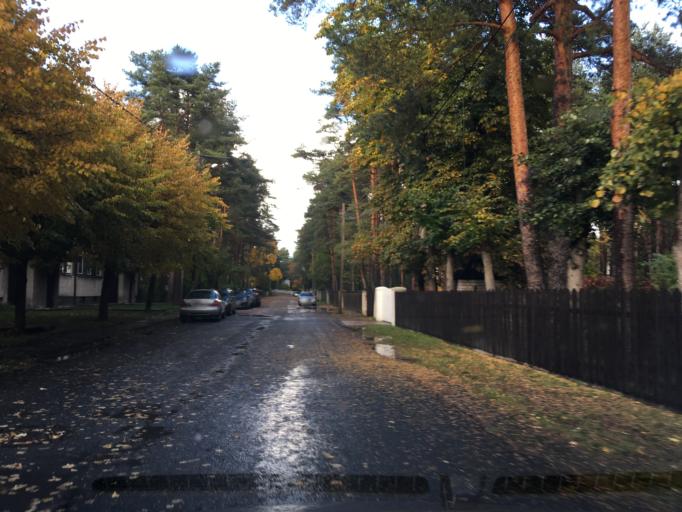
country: EE
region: Harju
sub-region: Tallinna linn
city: Tallinn
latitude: 59.3784
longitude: 24.7114
